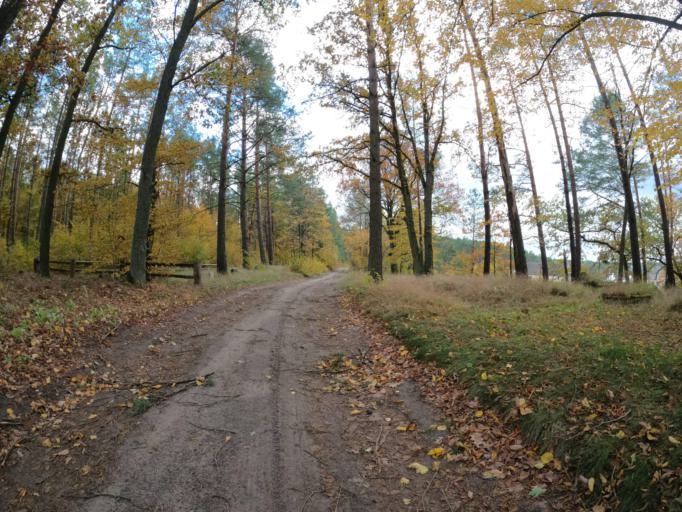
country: PL
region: West Pomeranian Voivodeship
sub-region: Powiat mysliborski
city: Barlinek
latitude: 52.9210
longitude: 15.2911
